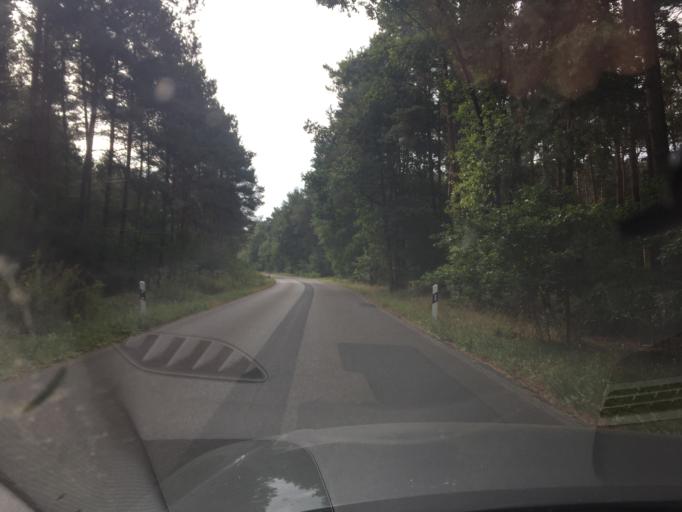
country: DE
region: Brandenburg
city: Erkner
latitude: 52.3965
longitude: 13.7642
